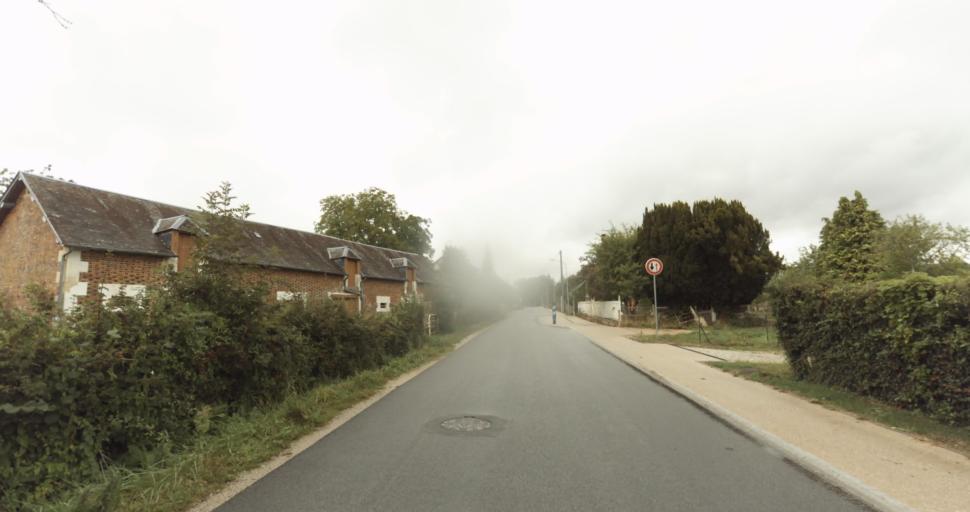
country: FR
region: Lower Normandy
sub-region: Departement de l'Orne
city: Vimoutiers
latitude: 48.9154
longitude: 0.2010
